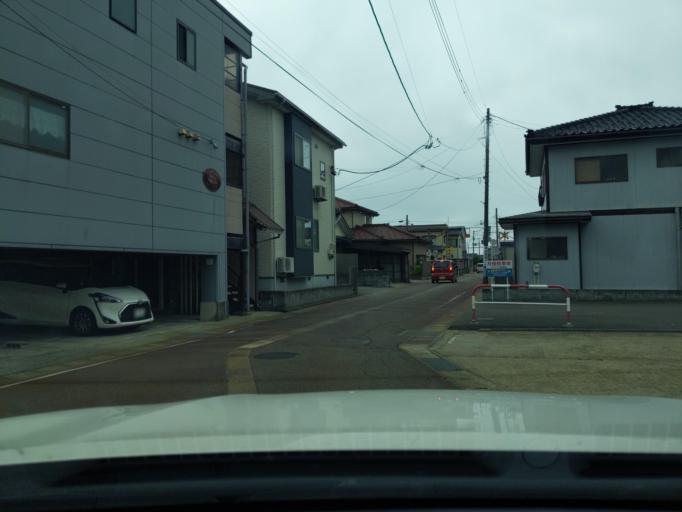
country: JP
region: Niigata
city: Kashiwazaki
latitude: 37.3714
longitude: 138.5659
